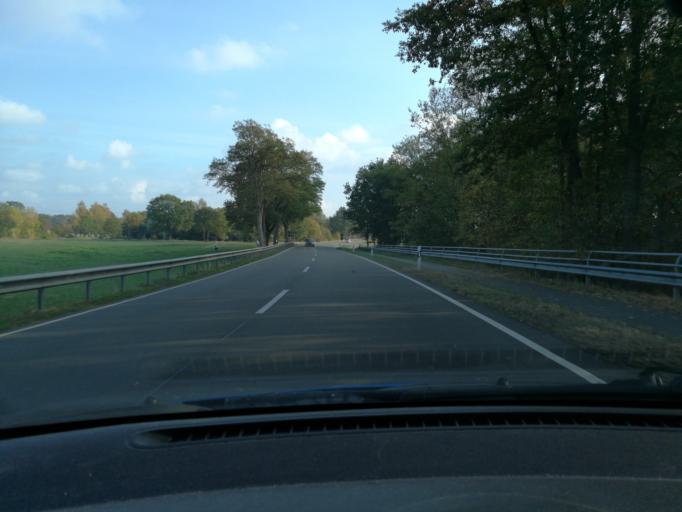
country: DE
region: Lower Saxony
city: Luechow
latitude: 52.9937
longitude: 11.1144
